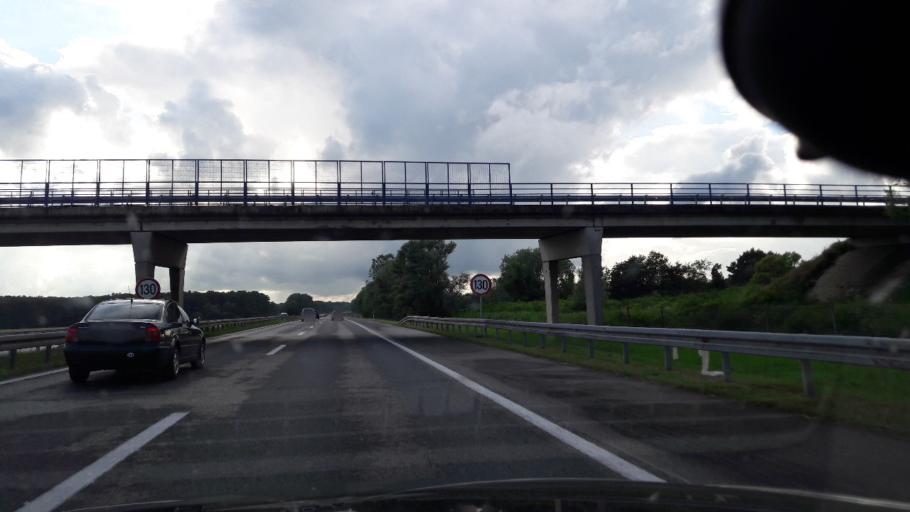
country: HR
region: Brodsko-Posavska
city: Okucani
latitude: 45.2907
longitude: 17.0900
